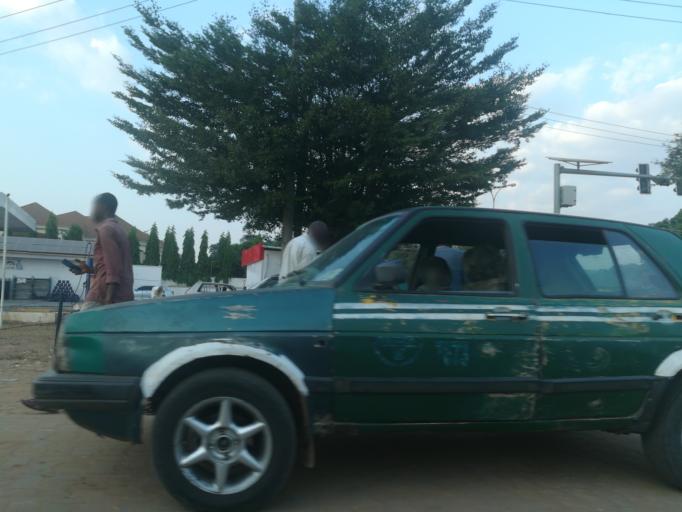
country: NG
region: Abuja Federal Capital Territory
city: Abuja
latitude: 9.0648
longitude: 7.4117
